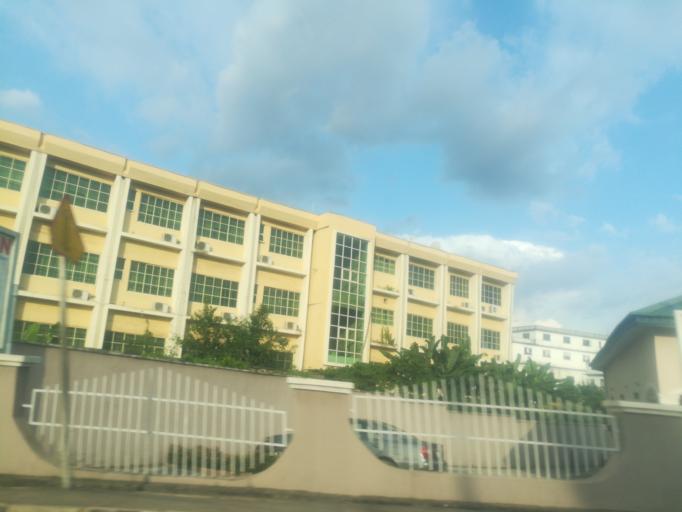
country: NG
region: Oyo
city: Ibadan
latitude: 7.3844
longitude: 3.8813
